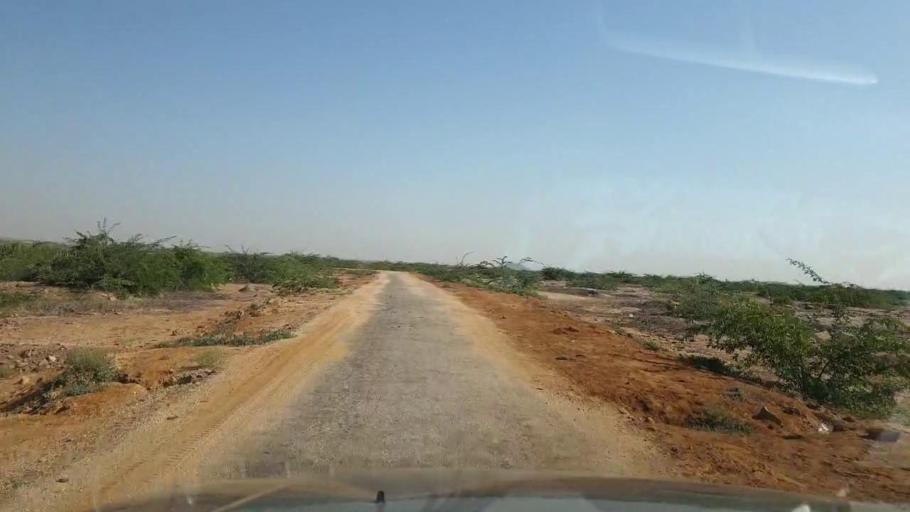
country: PK
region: Sindh
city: Thatta
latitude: 24.8796
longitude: 67.7952
